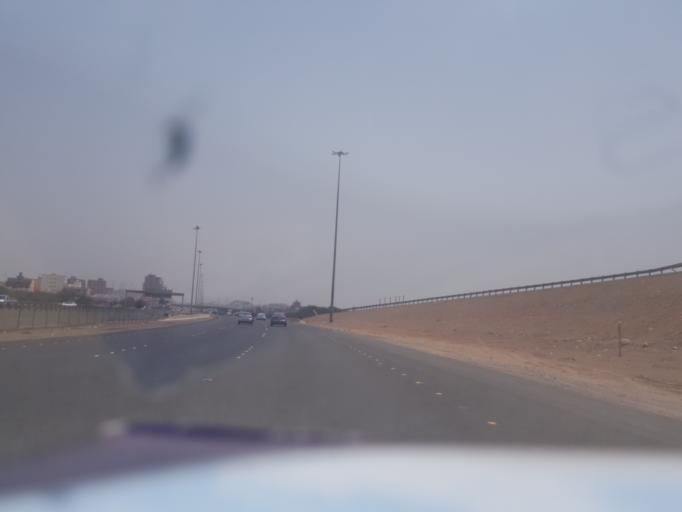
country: SA
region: Makkah
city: Jeddah
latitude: 21.4448
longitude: 39.2712
